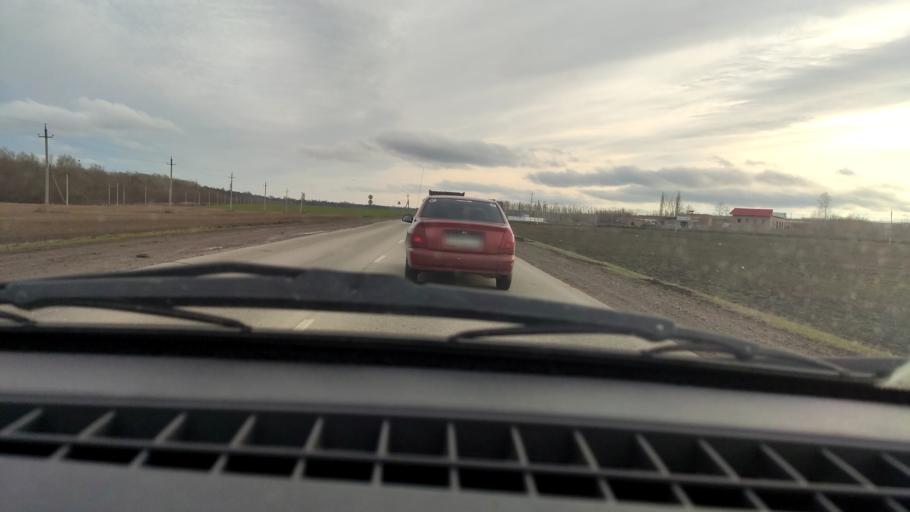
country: RU
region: Bashkortostan
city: Chishmy
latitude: 54.5700
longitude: 55.3538
